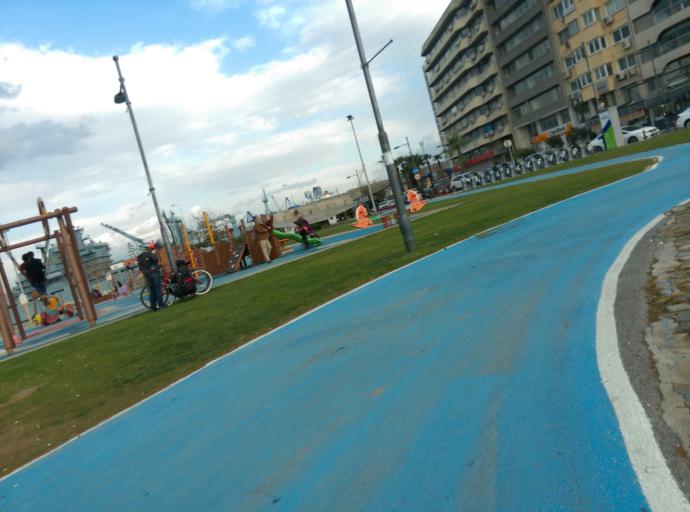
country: TR
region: Izmir
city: Izmir
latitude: 38.4423
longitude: 27.1429
